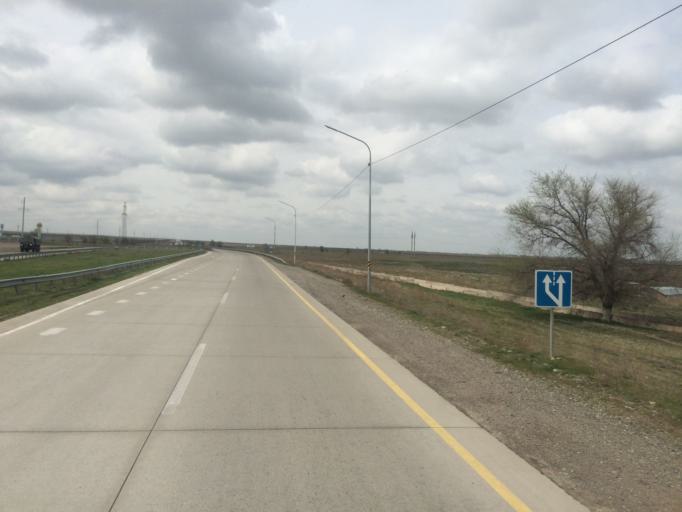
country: KZ
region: Zhambyl
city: Sarykemer
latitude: 43.0093
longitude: 71.7955
